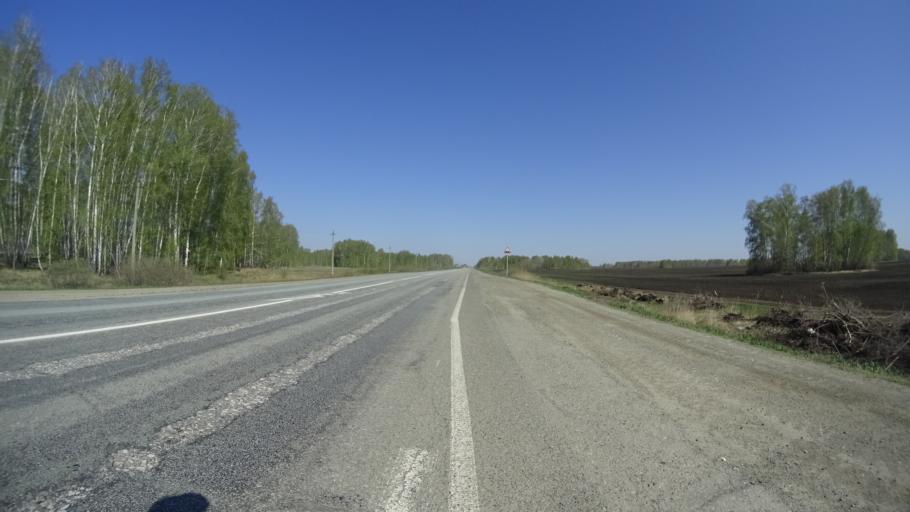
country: RU
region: Chelyabinsk
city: Troitsk
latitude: 54.1783
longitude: 61.4352
